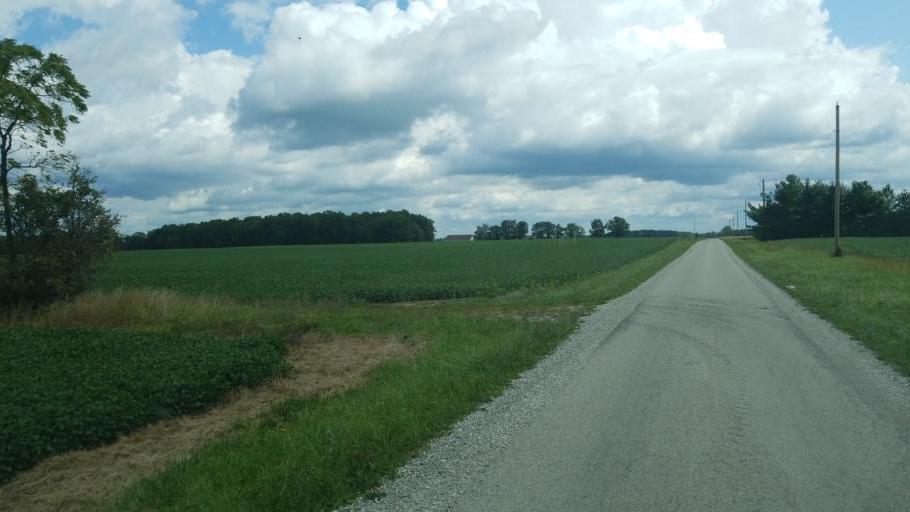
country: US
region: Ohio
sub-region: Huron County
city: Willard
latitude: 41.0953
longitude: -82.8521
